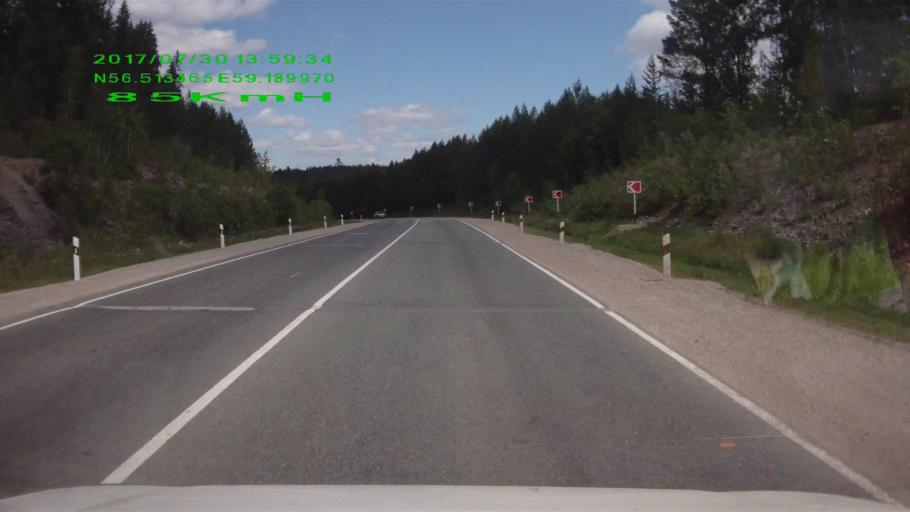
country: RU
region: Sverdlovsk
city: Mikhaylovsk
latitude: 56.5136
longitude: 59.1904
